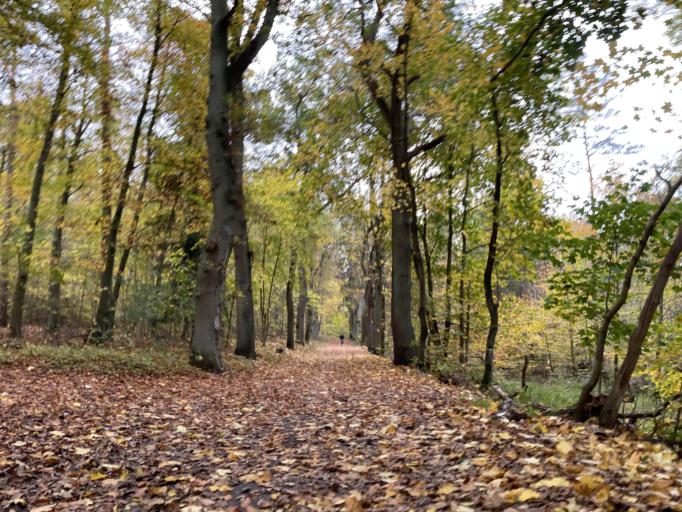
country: DE
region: Lower Saxony
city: Lueneburg
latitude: 53.2197
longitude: 10.3977
